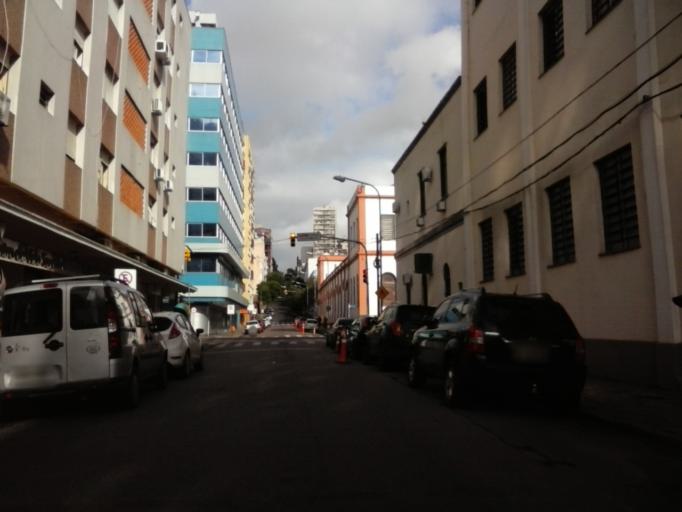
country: BR
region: Rio Grande do Sul
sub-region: Porto Alegre
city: Porto Alegre
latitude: -30.0306
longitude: -51.2357
